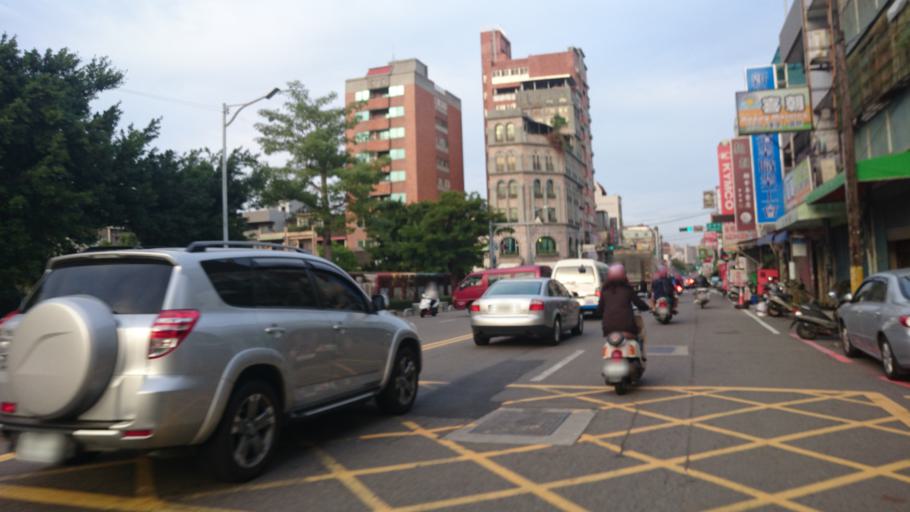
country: TW
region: Taiwan
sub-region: Hsinchu
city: Hsinchu
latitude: 24.7959
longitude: 120.9744
